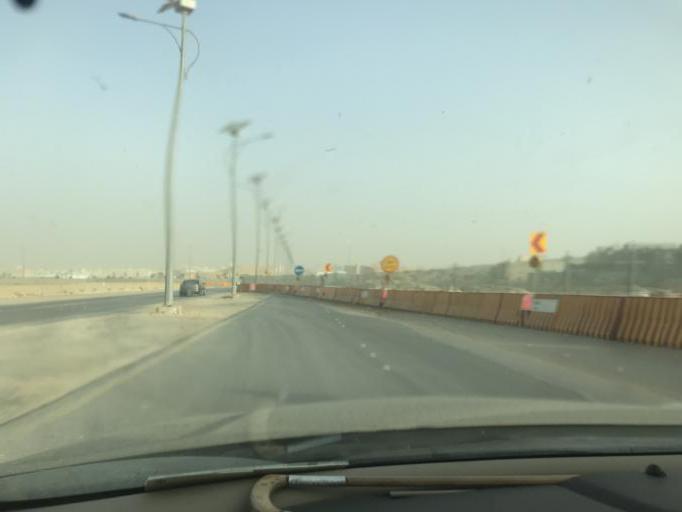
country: SA
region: Ar Riyad
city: Riyadh
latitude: 24.8440
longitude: 46.6652
